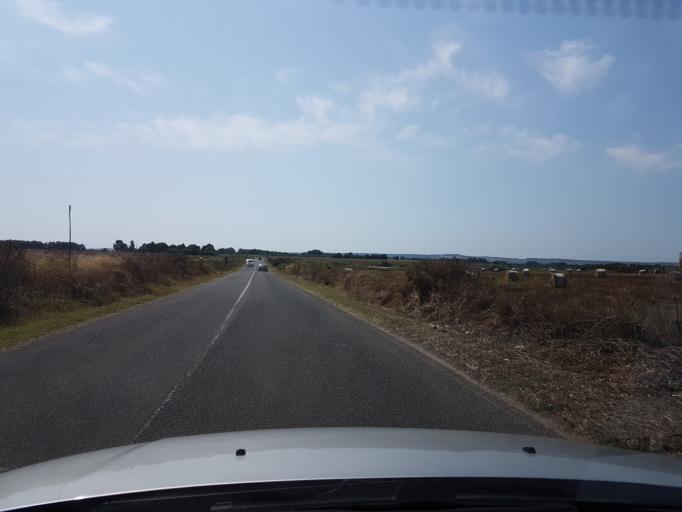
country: IT
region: Sardinia
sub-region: Provincia di Oristano
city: Cabras
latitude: 39.9188
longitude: 8.5140
